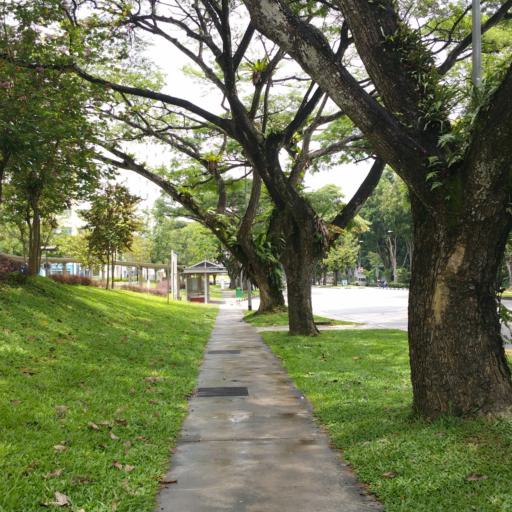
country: MY
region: Johor
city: Kampung Pasir Gudang Baru
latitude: 1.4208
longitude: 103.8486
